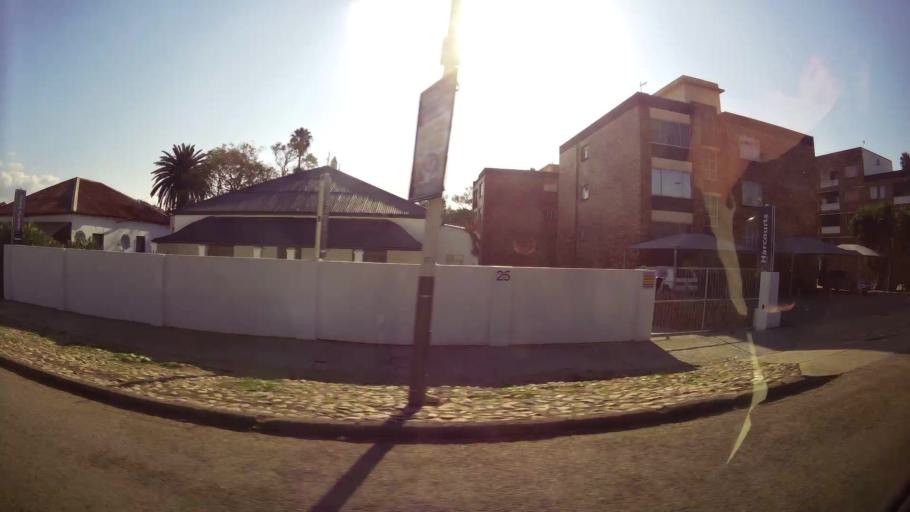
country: ZA
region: Eastern Cape
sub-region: Nelson Mandela Bay Metropolitan Municipality
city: Uitenhage
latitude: -33.7623
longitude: 25.4033
